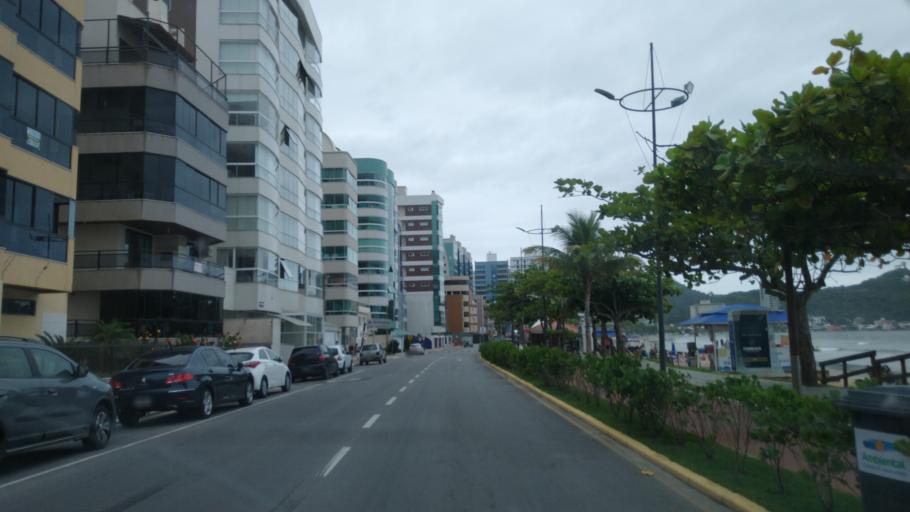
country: BR
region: Santa Catarina
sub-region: Itapema
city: Itapema
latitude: -27.0993
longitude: -48.6141
